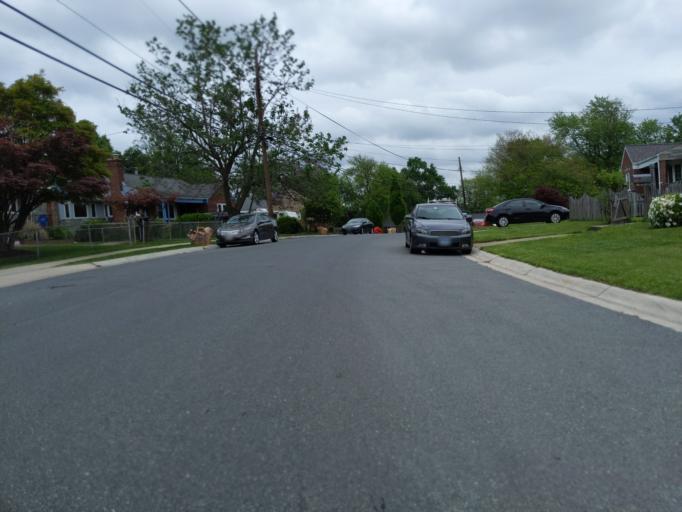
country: US
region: Maryland
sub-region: Montgomery County
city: Forest Glen
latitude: 39.0231
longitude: -77.0476
